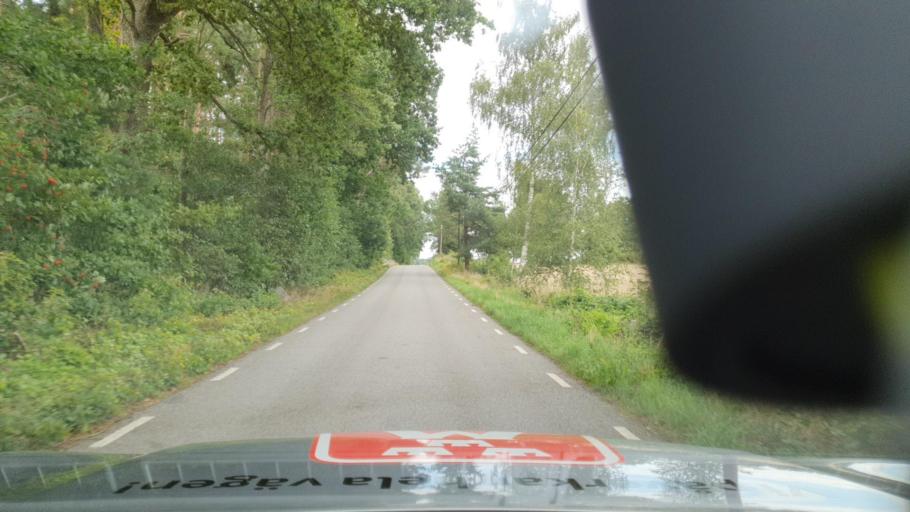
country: SE
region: Kalmar
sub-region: Kalmar Kommun
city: Lindsdal
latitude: 56.7746
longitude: 16.2526
